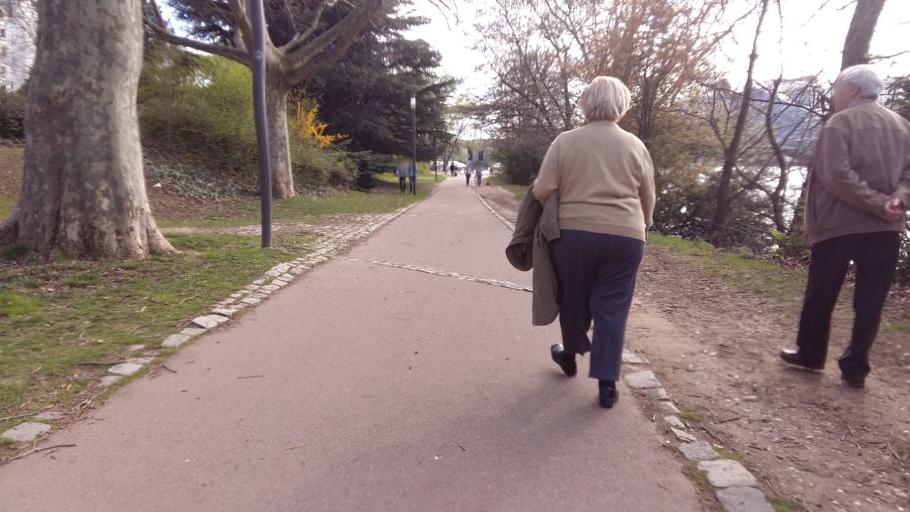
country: FR
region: Rhone-Alpes
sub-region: Departement du Rhone
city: La Mulatiere
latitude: 45.7355
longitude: 4.8227
